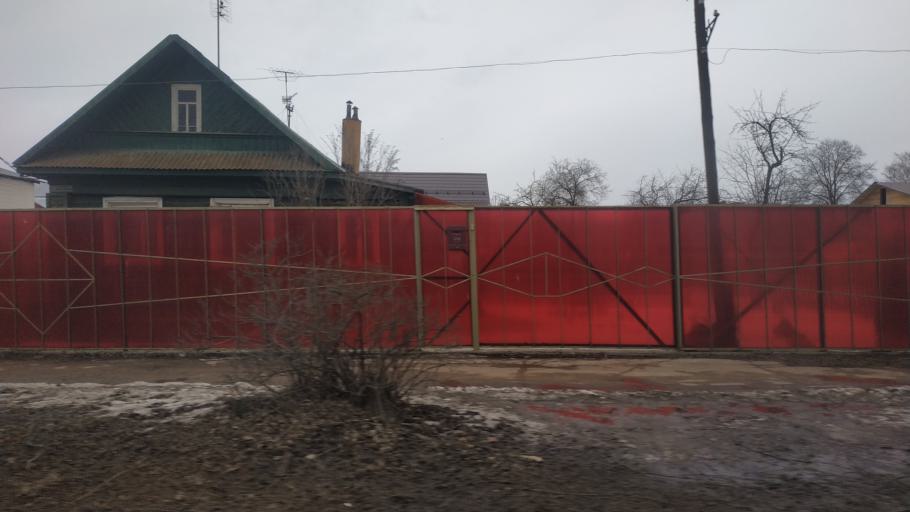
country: RU
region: Tverskaya
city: Tver
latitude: 56.8804
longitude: 35.8895
